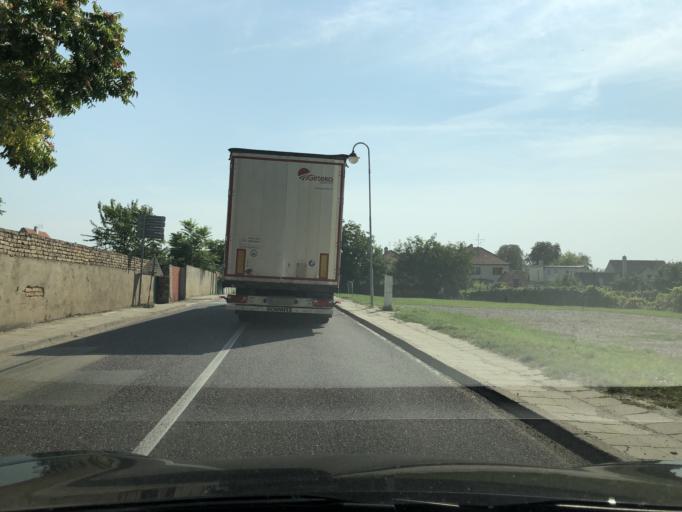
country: CZ
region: South Moravian
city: Brezi
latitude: 48.8201
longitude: 16.5659
